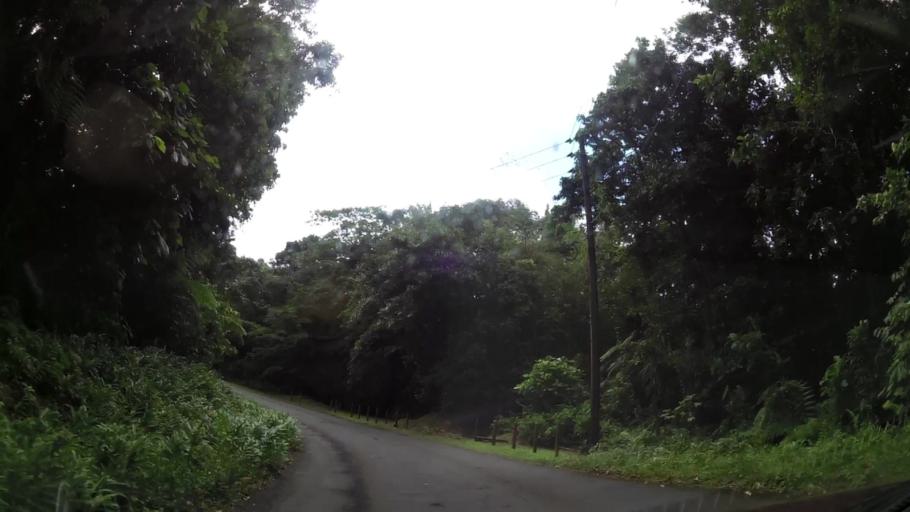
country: DM
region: Saint Paul
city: Pont Casse
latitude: 15.3974
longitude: -61.3110
